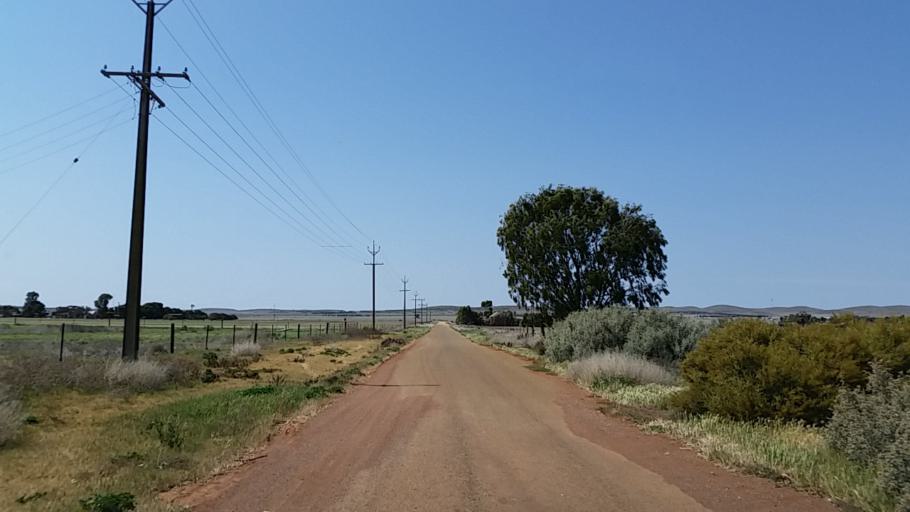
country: AU
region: South Australia
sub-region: Peterborough
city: Peterborough
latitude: -32.9595
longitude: 138.8495
